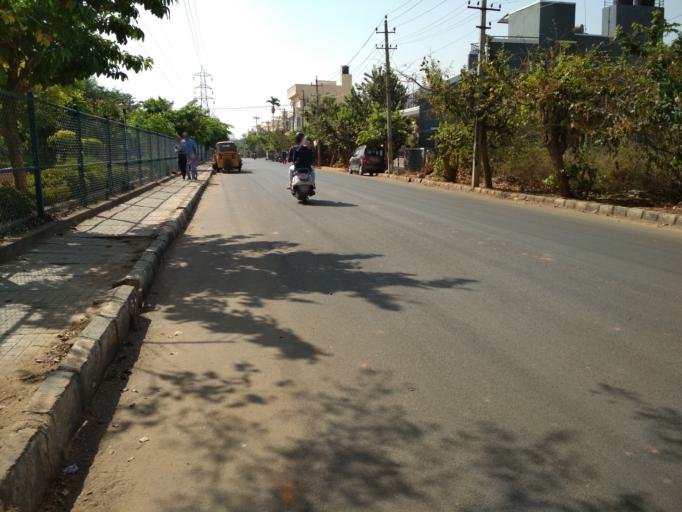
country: IN
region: Karnataka
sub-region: Bangalore Urban
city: Yelahanka
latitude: 13.0707
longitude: 77.5774
